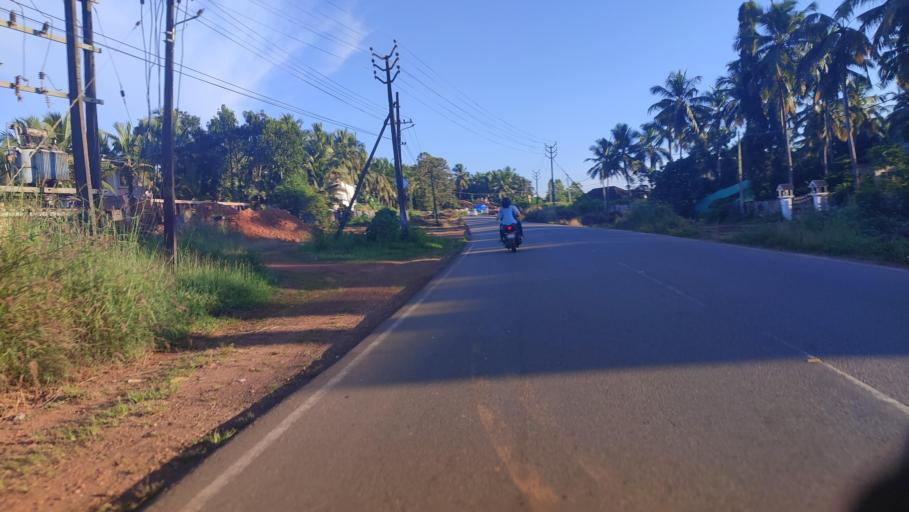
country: IN
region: Kerala
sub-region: Kasaragod District
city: Kasaragod
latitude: 12.4755
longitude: 75.0588
